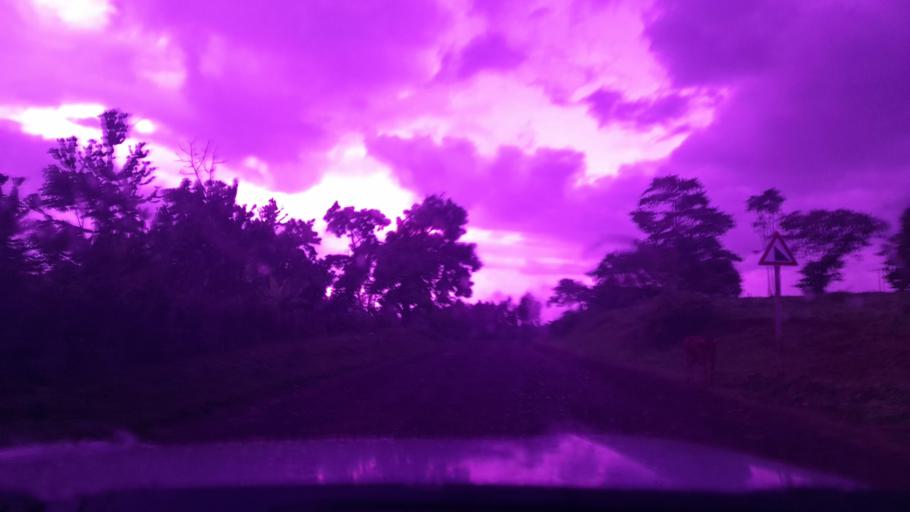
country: ET
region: Southern Nations, Nationalities, and People's Region
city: Mizan Teferi
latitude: 6.9161
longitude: 35.8416
